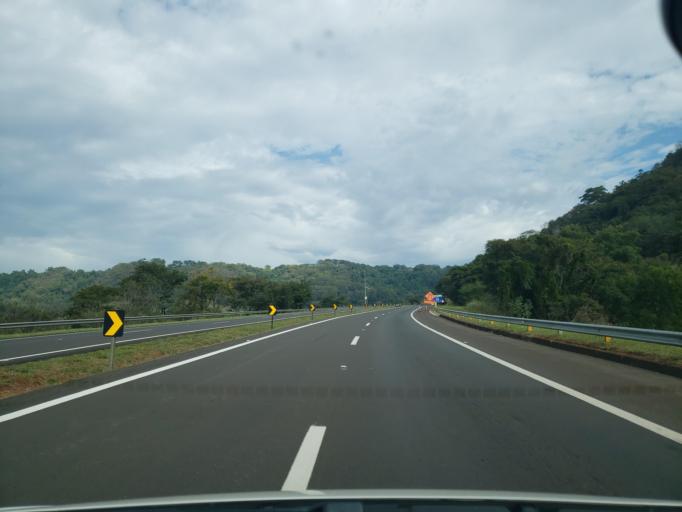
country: BR
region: Sao Paulo
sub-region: Dois Corregos
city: Dois Corregos
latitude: -22.2490
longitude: -48.3355
